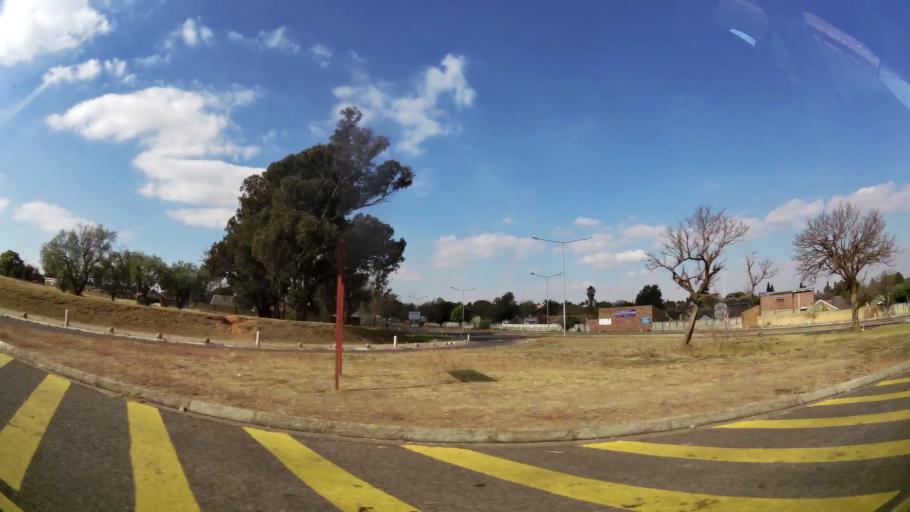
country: ZA
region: Gauteng
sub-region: West Rand District Municipality
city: Krugersdorp
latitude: -26.0811
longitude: 27.7599
